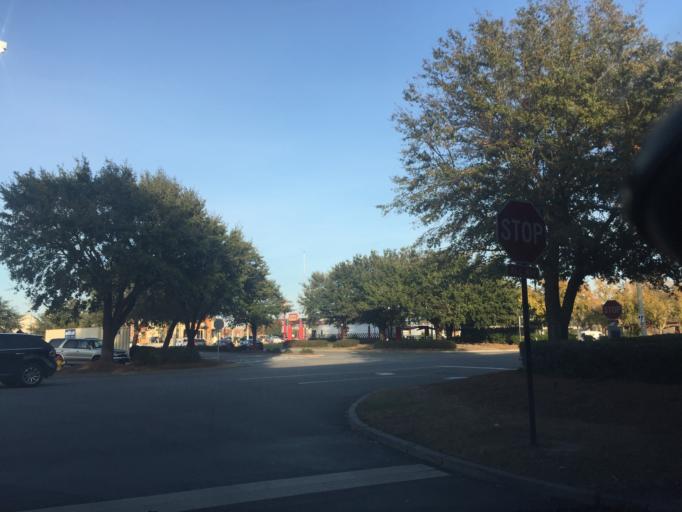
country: US
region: Georgia
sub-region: Chatham County
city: Isle of Hope
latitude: 32.0037
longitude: -81.1150
